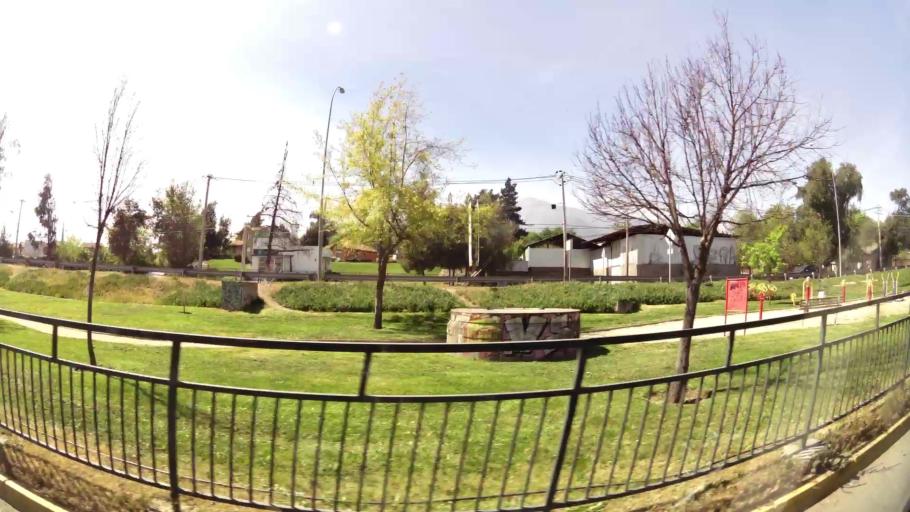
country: CL
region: Santiago Metropolitan
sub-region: Provincia de Cordillera
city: Puente Alto
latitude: -33.5953
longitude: -70.5368
